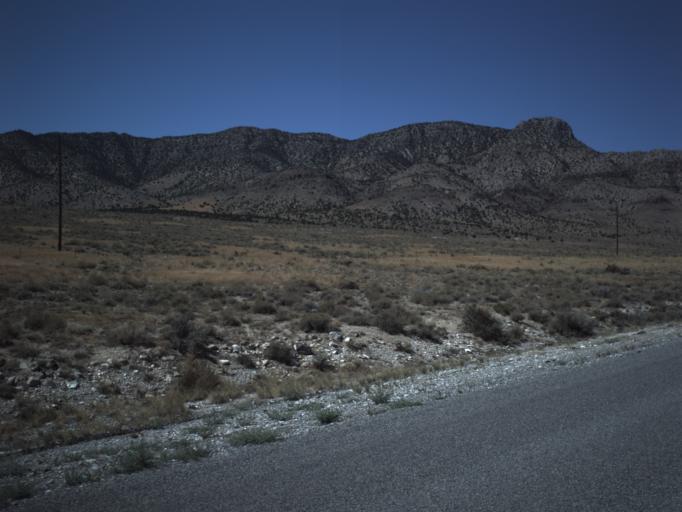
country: US
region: Utah
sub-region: Beaver County
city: Milford
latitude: 39.0862
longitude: -113.5292
